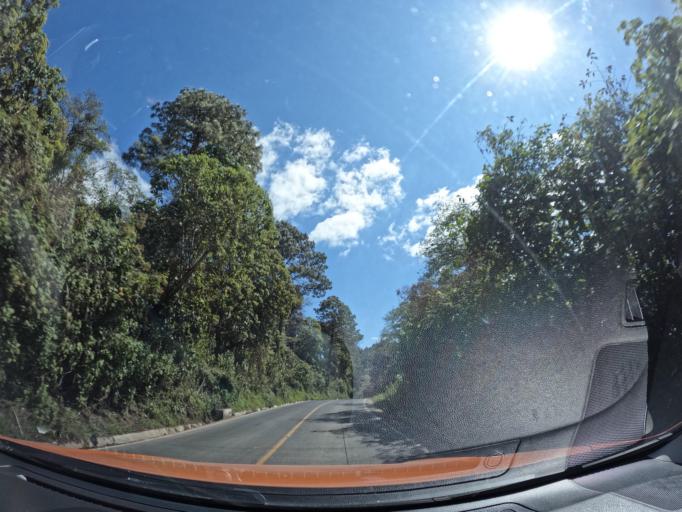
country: GT
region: Chimaltenango
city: Patzun
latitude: 14.6504
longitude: -91.0466
